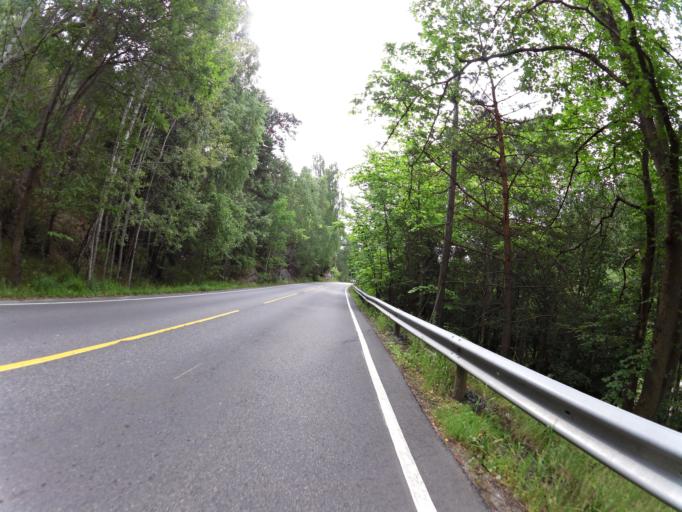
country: NO
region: Akershus
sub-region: Oppegard
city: Kolbotn
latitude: 59.8270
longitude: 10.7690
